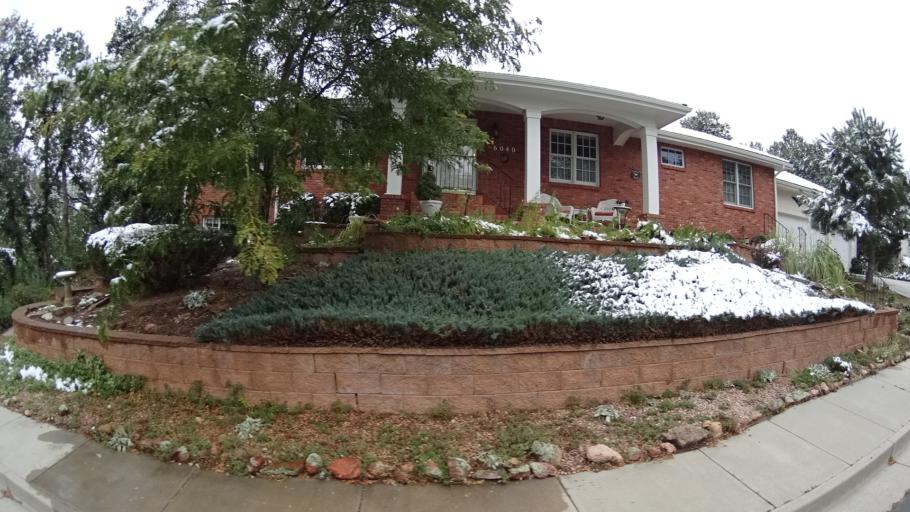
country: US
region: Colorado
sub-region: El Paso County
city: Colorado Springs
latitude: 38.9160
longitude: -104.8010
